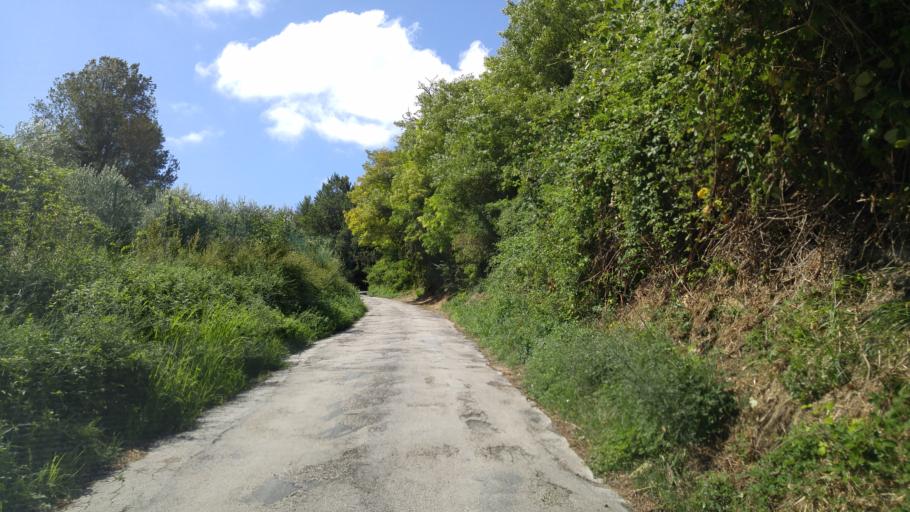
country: IT
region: The Marches
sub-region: Provincia di Pesaro e Urbino
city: Fenile
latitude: 43.8241
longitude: 12.9693
